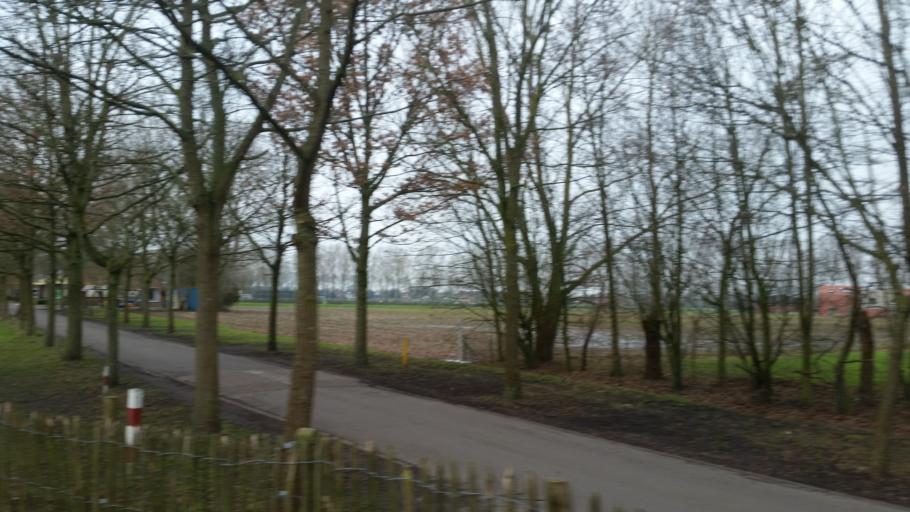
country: BE
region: Flanders
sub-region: Provincie West-Vlaanderen
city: Sint-Kruis
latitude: 51.2203
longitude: 3.2536
